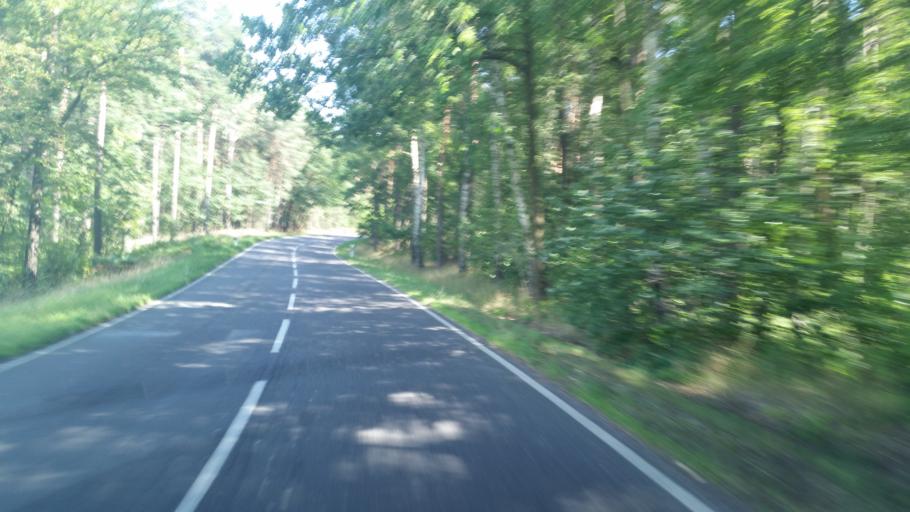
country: DE
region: Saxony
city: Neukirch
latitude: 51.3055
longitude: 14.0412
